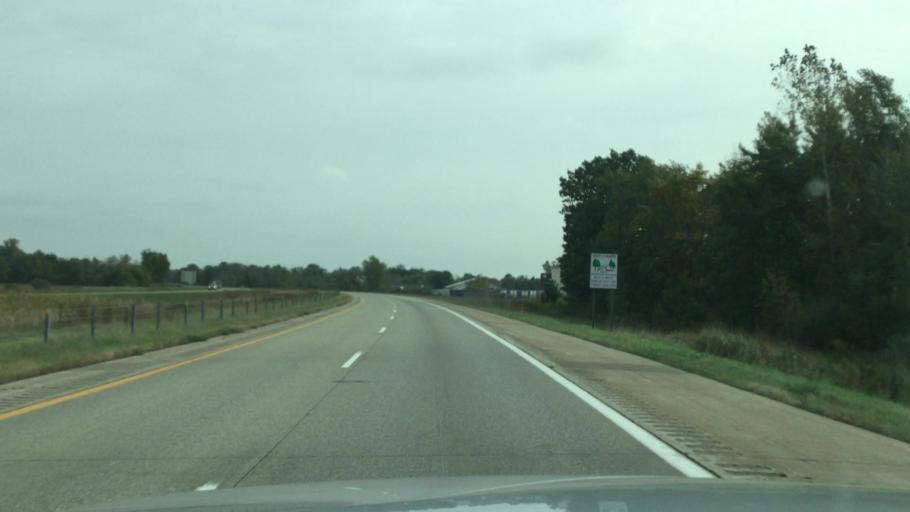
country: US
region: Michigan
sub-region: Shiawassee County
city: Perry
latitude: 42.8414
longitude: -84.2023
